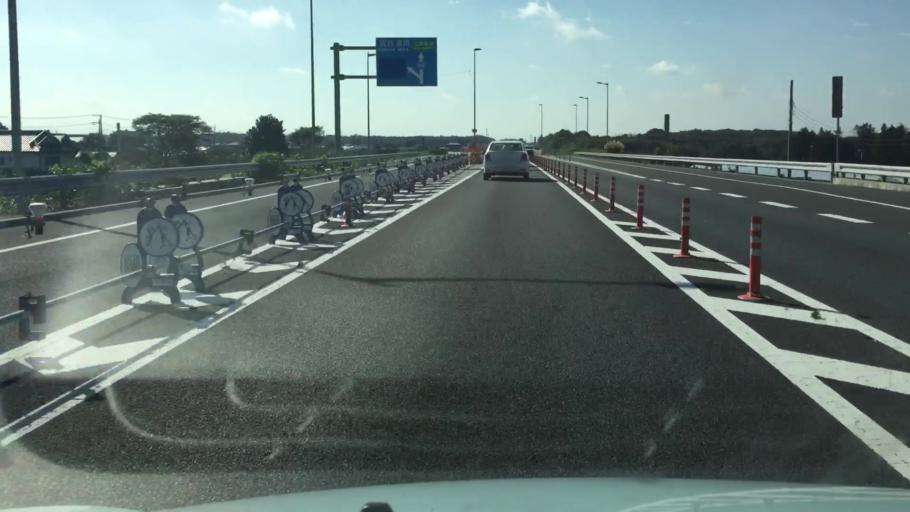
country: JP
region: Tochigi
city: Mooka
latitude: 36.5153
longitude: 139.9862
